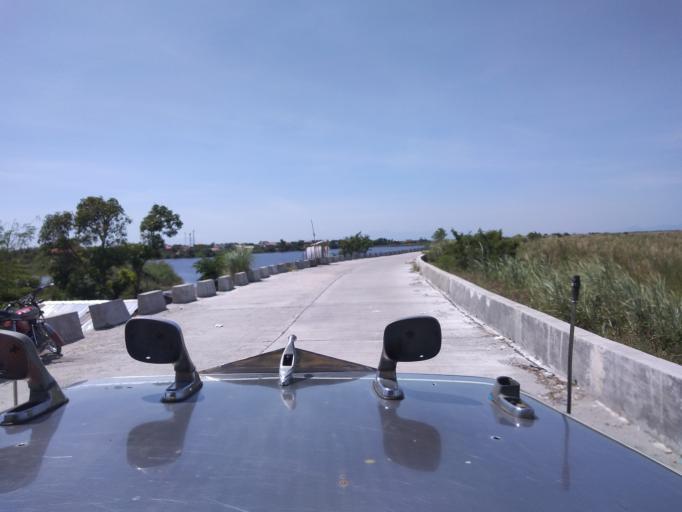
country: PH
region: Central Luzon
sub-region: Province of Pampanga
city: Minalin
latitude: 14.9859
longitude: 120.6941
